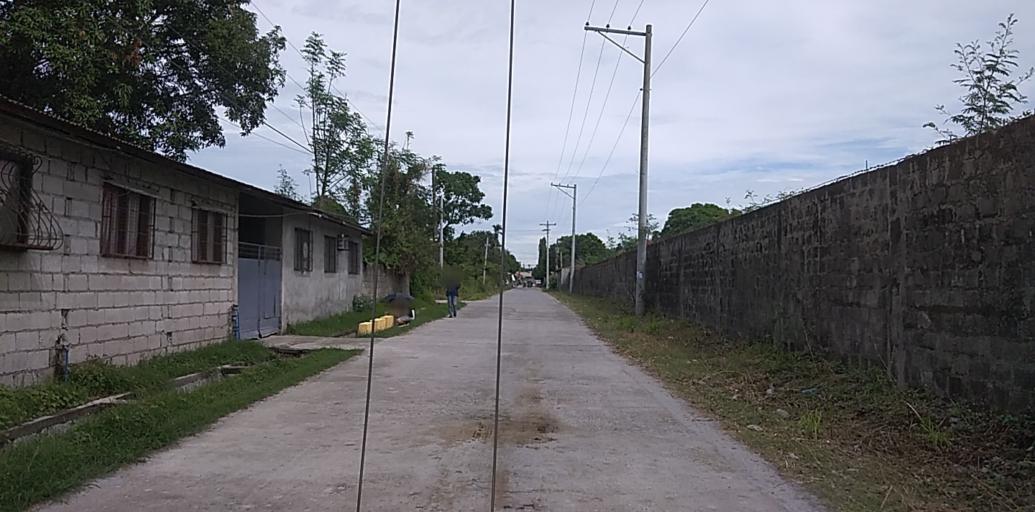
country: PH
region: Central Luzon
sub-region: Province of Pampanga
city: Manibaug Pasig
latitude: 15.1102
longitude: 120.5597
